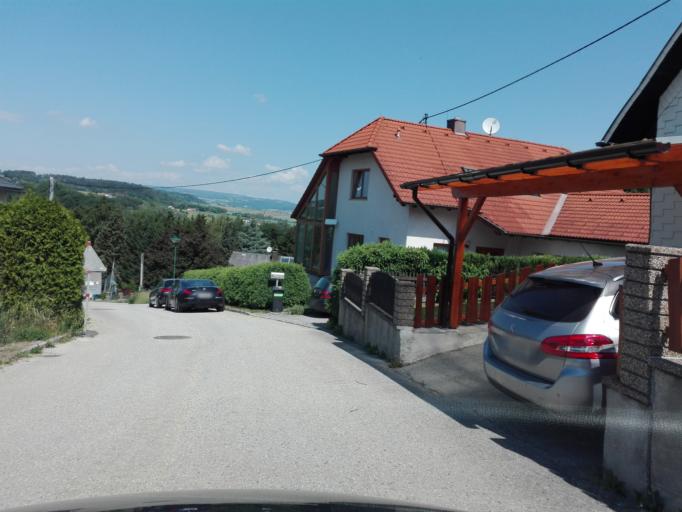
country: AT
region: Upper Austria
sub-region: Politischer Bezirk Urfahr-Umgebung
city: Engerwitzdorf
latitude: 48.2847
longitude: 14.4719
